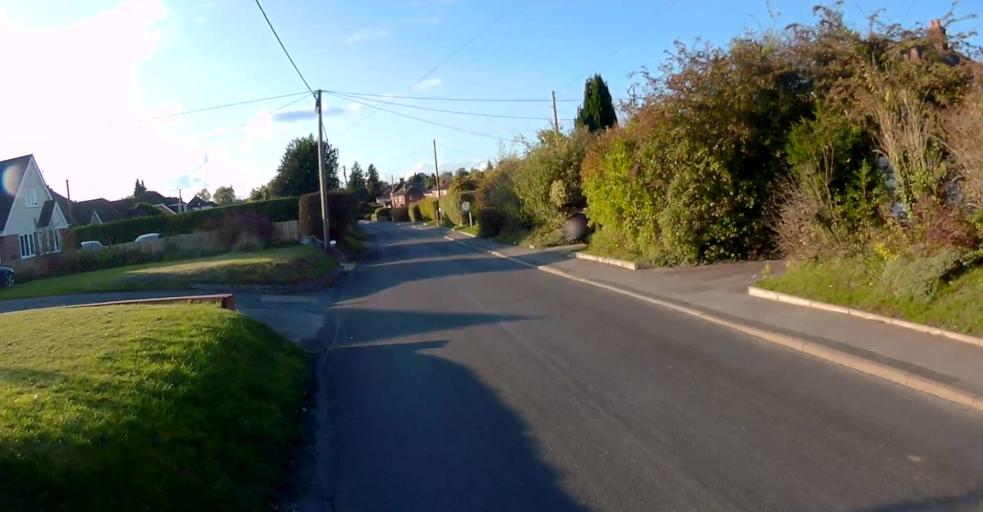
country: GB
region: England
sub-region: Hampshire
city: Old Basing
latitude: 51.2665
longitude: -1.0385
